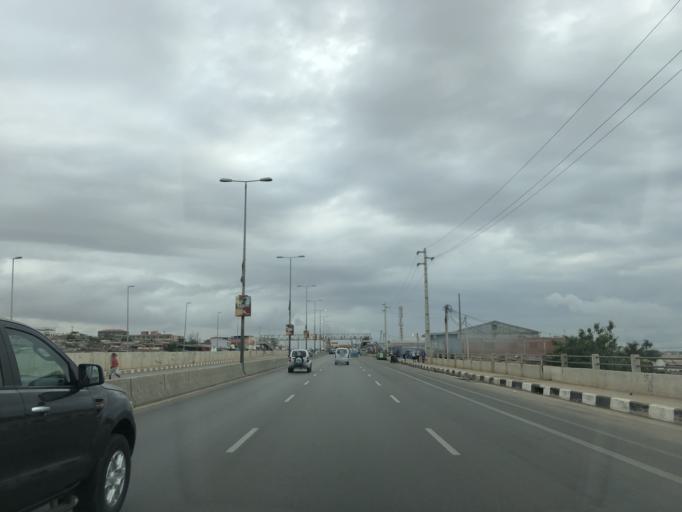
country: AO
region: Luanda
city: Luanda
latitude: -8.8595
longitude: 13.2163
